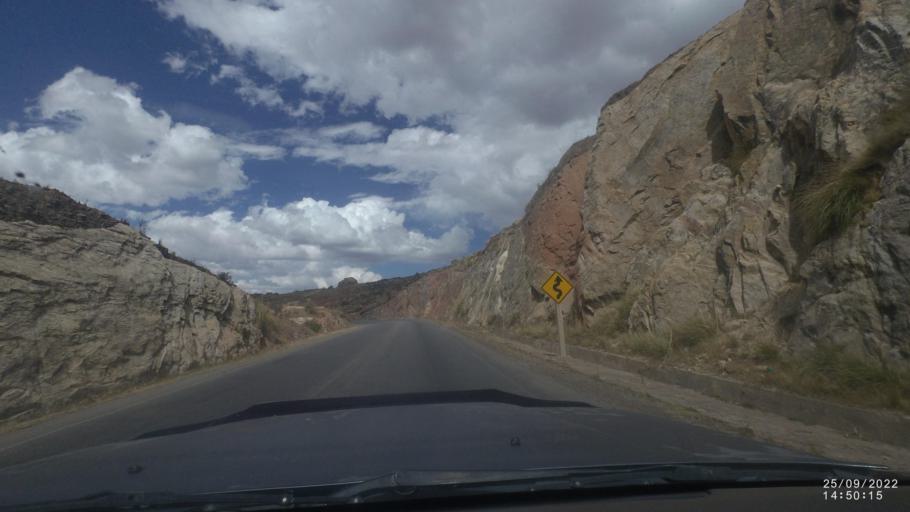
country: BO
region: Cochabamba
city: Irpa Irpa
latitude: -17.7023
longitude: -66.4825
